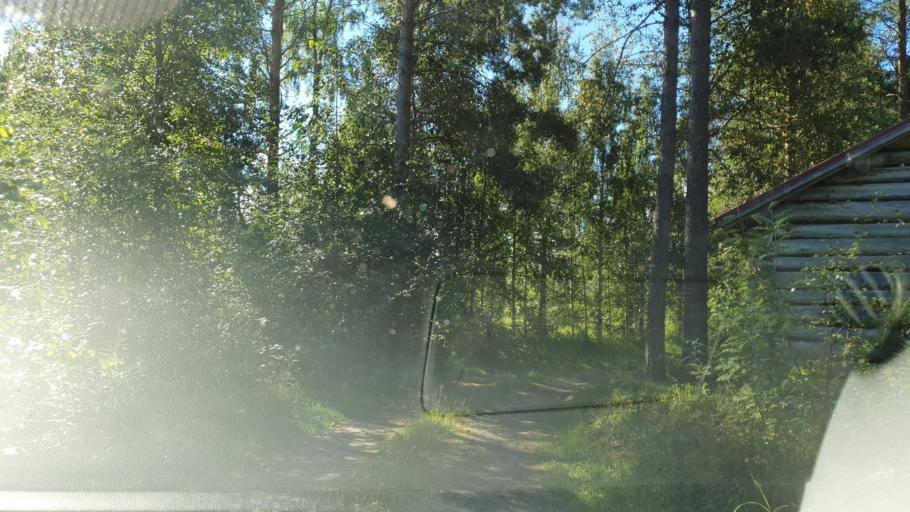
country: FI
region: Kainuu
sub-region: Kehys-Kainuu
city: Kuhmo
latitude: 64.1285
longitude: 29.3977
